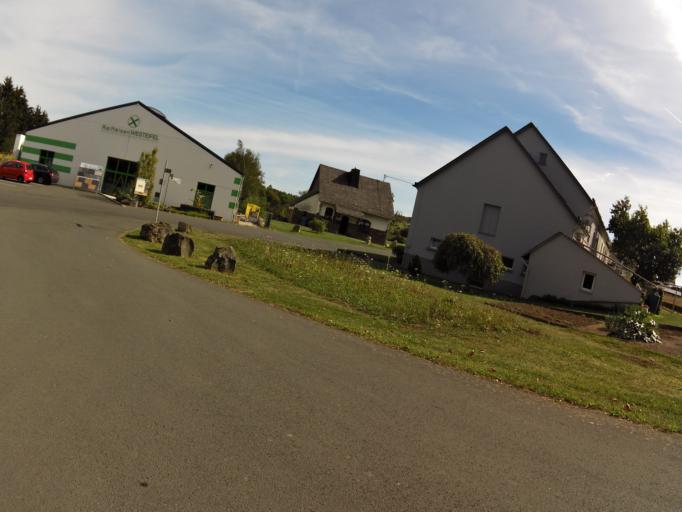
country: DE
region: Rheinland-Pfalz
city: Euscheid
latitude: 50.1277
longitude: 6.2669
